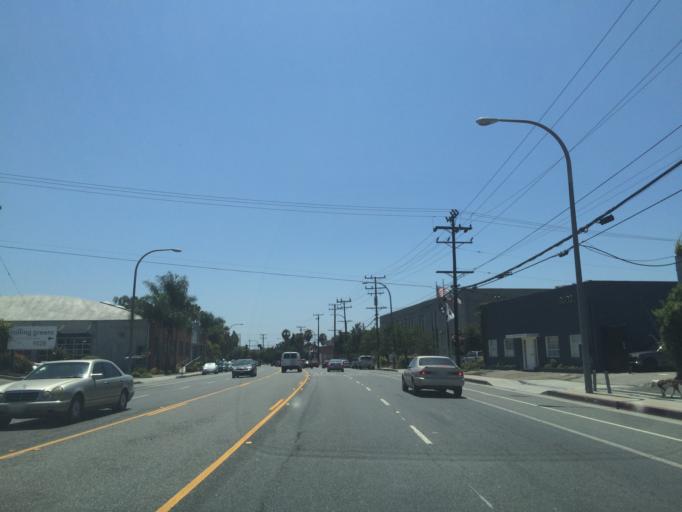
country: US
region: California
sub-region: Los Angeles County
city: Culver City
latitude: 34.0184
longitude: -118.3868
